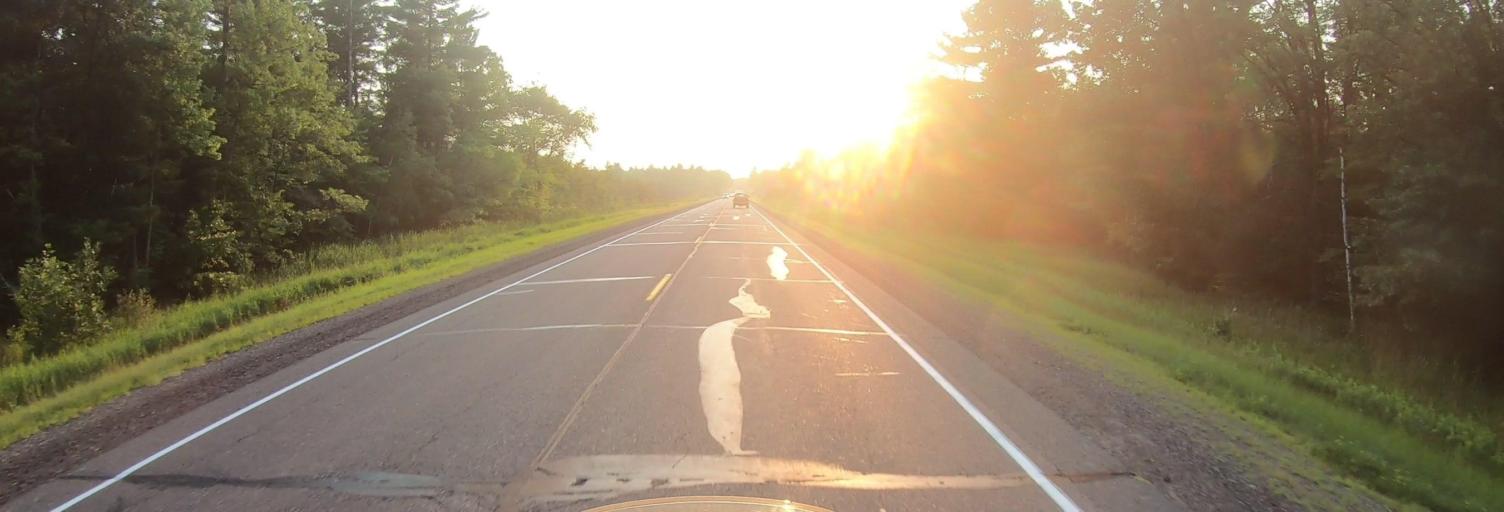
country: US
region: Wisconsin
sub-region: Polk County
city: Frederic
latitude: 45.7705
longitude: -92.4967
